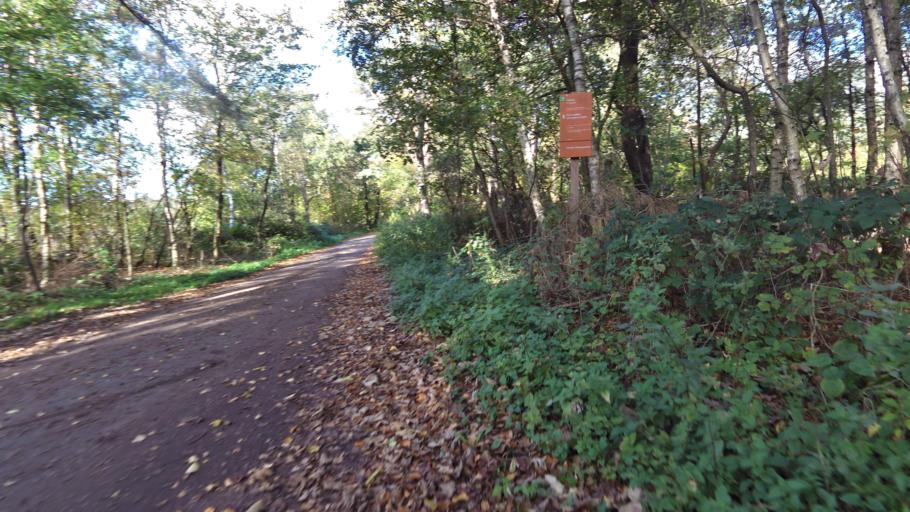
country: NL
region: Gelderland
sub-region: Gemeente Nunspeet
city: Nunspeet
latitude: 52.3373
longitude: 5.8310
